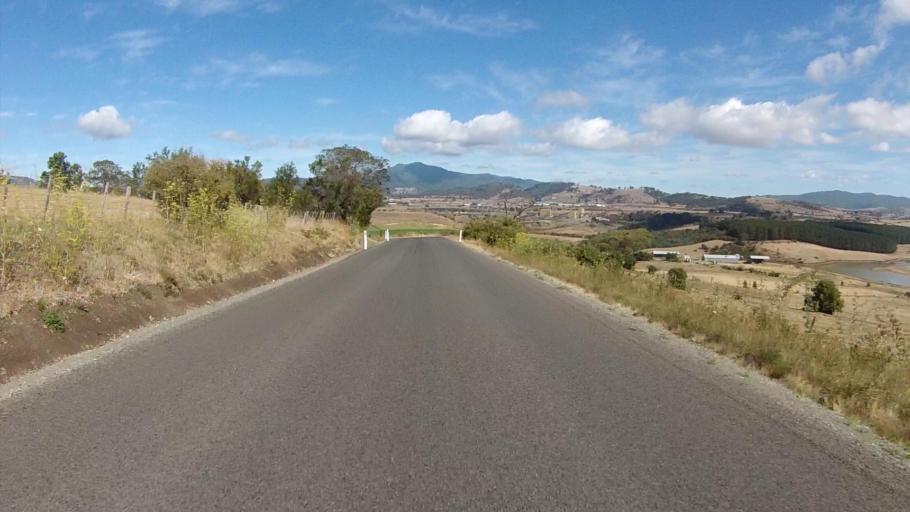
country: AU
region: Tasmania
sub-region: Brighton
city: Bridgewater
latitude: -42.7285
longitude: 147.2688
